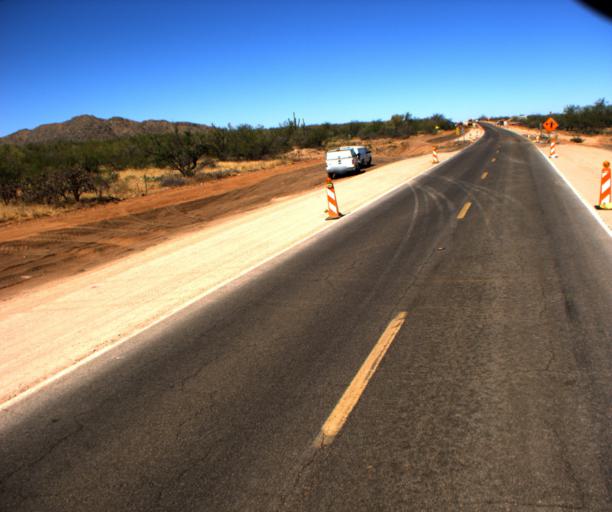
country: US
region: Arizona
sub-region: Pima County
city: Sells
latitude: 32.0079
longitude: -111.6730
